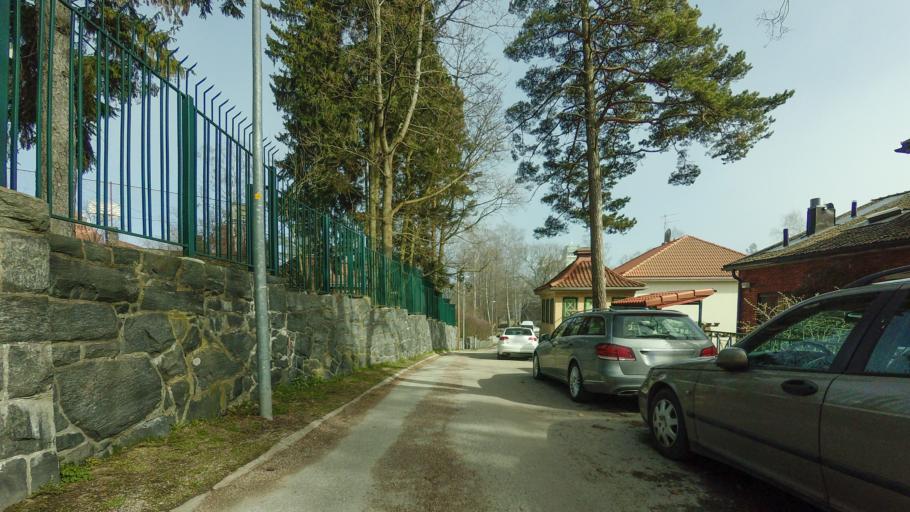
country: FI
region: Uusimaa
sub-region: Helsinki
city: Helsinki
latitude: 60.1826
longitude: 25.0057
